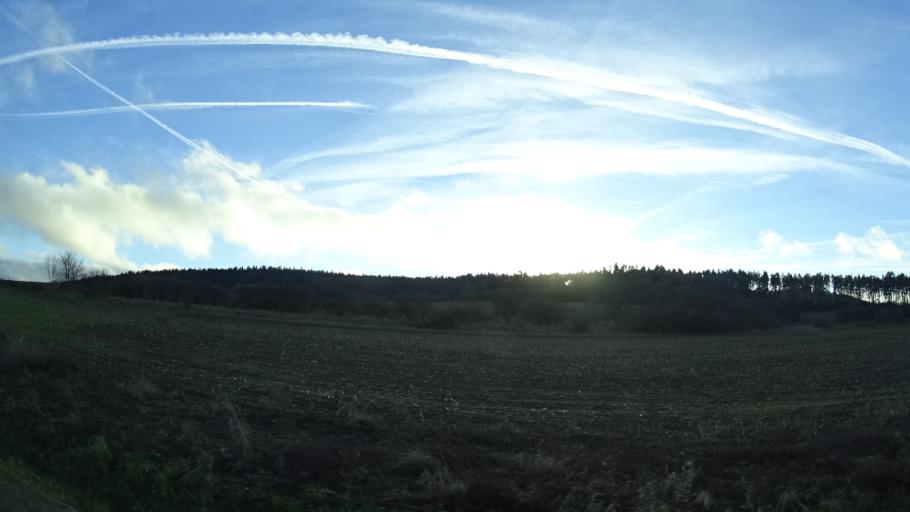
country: DE
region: Thuringia
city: Stadtilm
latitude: 50.7434
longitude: 11.1146
